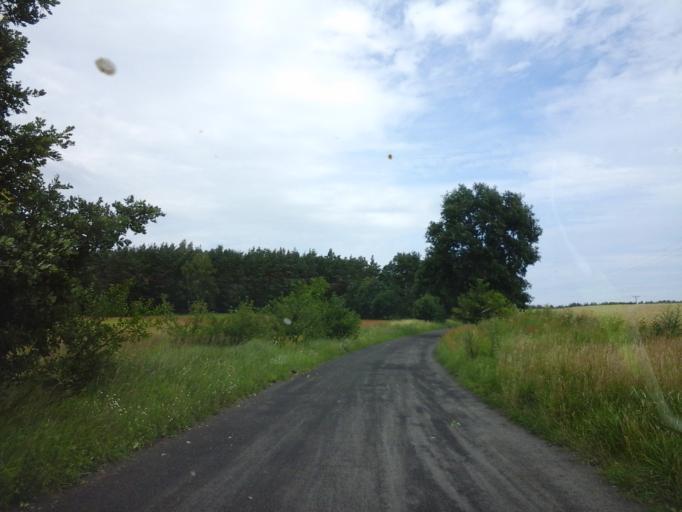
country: PL
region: Lubusz
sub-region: Powiat strzelecko-drezdenecki
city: Dobiegniew
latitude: 53.0216
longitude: 15.7437
